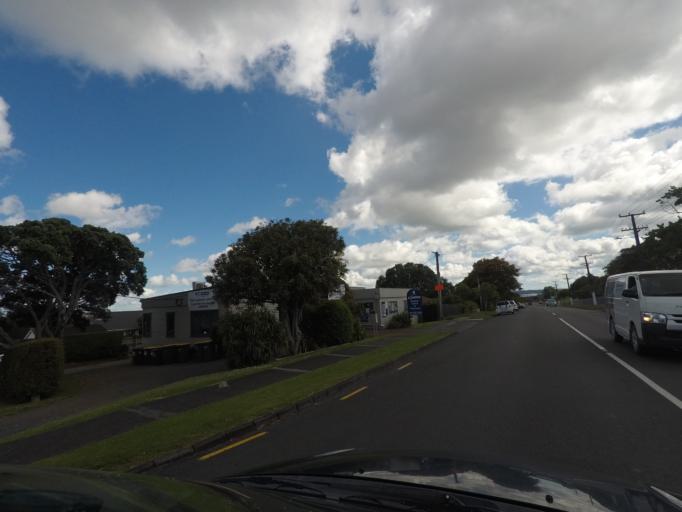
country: NZ
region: Auckland
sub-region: Auckland
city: Waitakere
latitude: -36.9059
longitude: 174.6637
